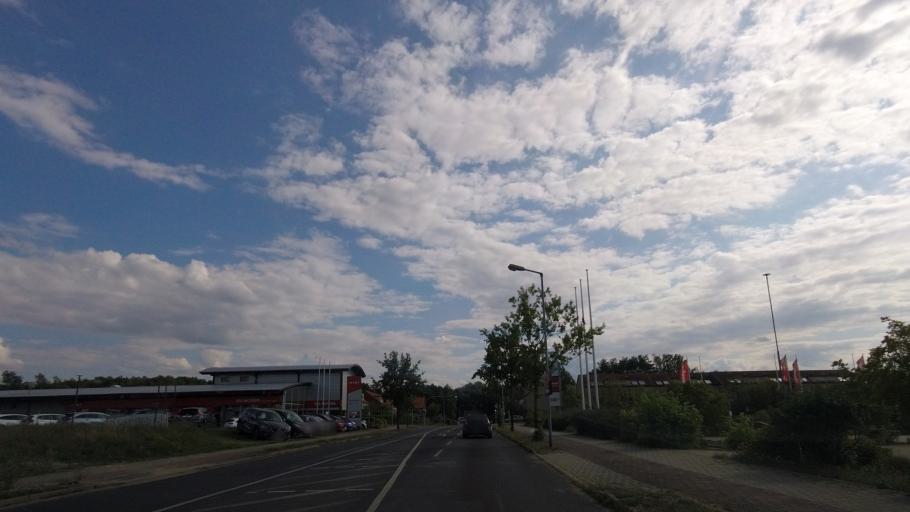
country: DE
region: Brandenburg
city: Erkner
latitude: 52.3954
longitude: 13.7199
